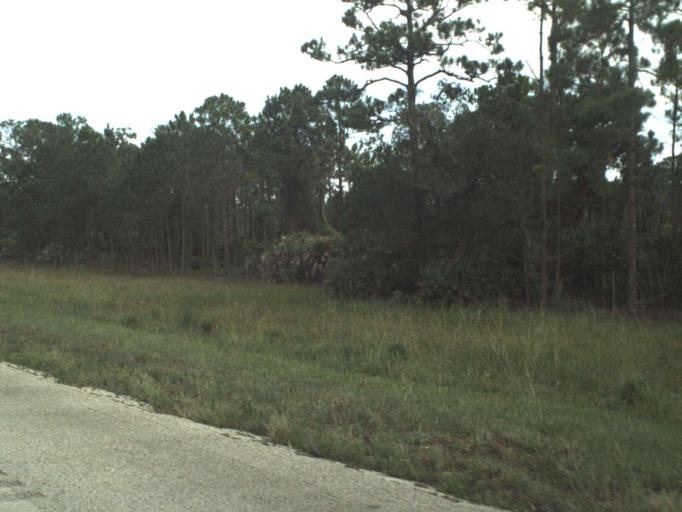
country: US
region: Florida
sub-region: Martin County
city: Palm City
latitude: 27.1359
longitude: -80.3604
